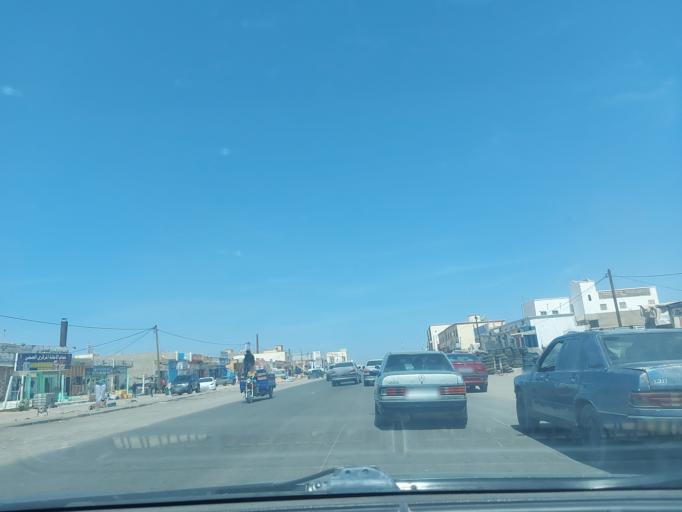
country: MR
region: Nouakchott
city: Nouakchott
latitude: 18.0739
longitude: -15.9462
